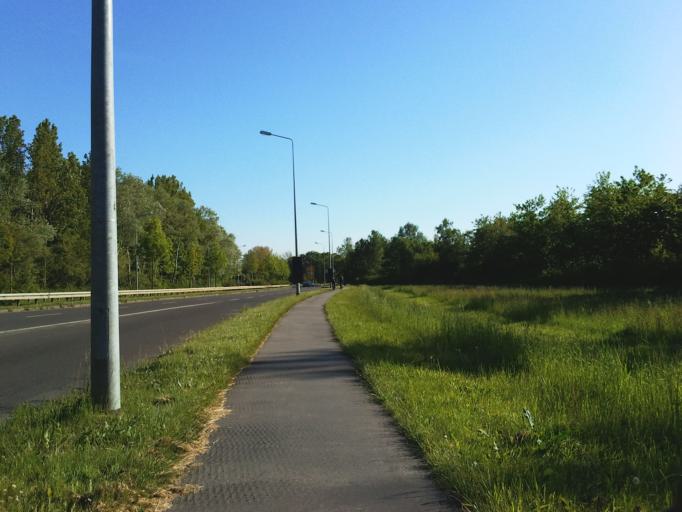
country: DE
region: Mecklenburg-Vorpommern
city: Warnemuende
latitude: 54.1449
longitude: 12.0648
